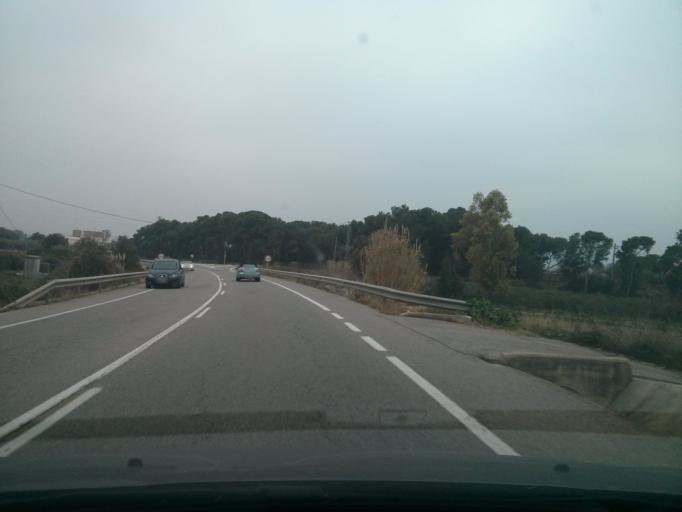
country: ES
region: Catalonia
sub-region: Provincia de Tarragona
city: Santa Oliva
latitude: 41.2620
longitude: 1.5503
